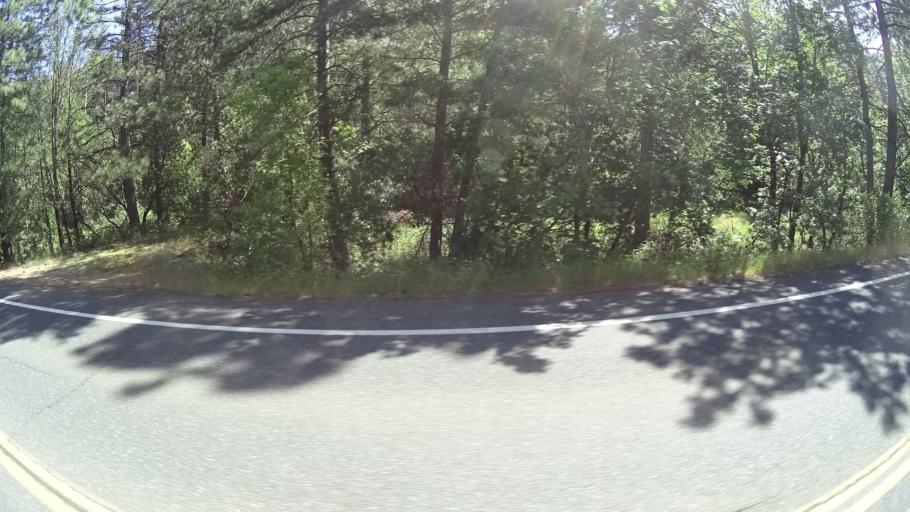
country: US
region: California
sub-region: Lake County
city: Cobb
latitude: 38.8177
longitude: -122.7150
